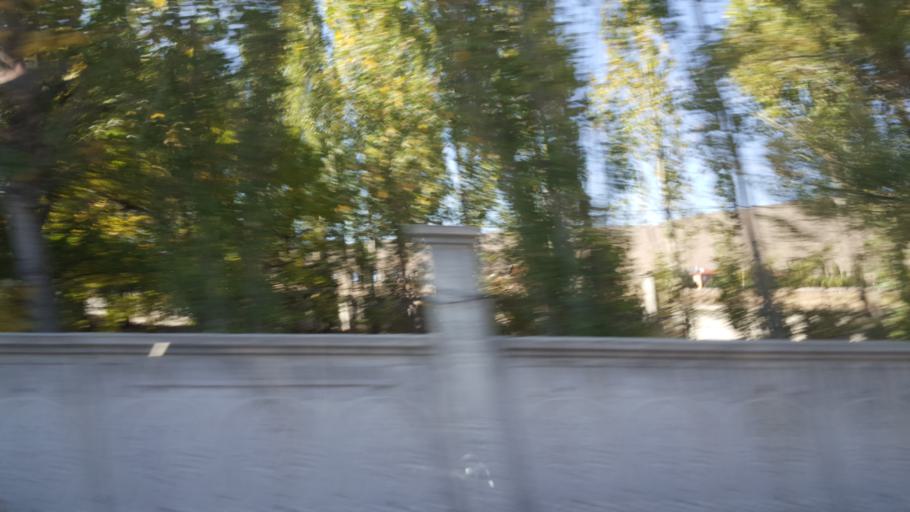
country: TR
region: Ankara
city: Altpinar
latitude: 39.1728
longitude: 32.7267
